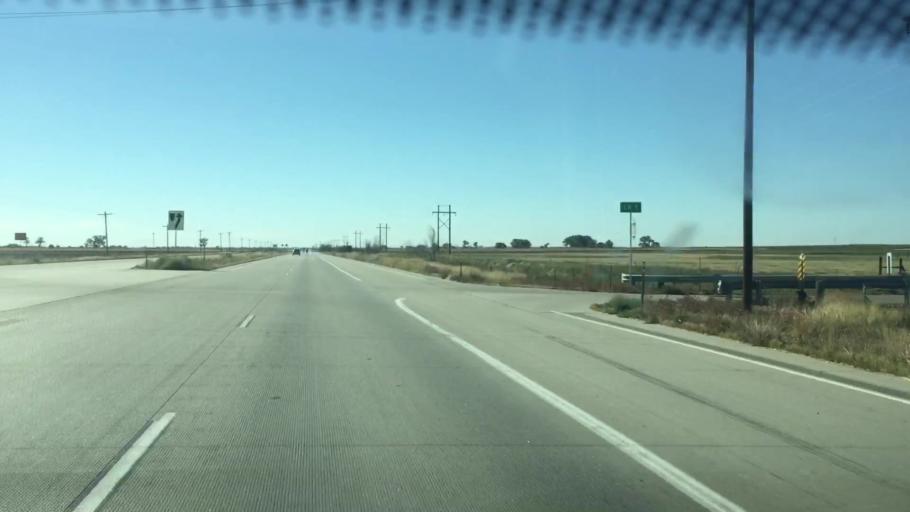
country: US
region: Colorado
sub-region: Prowers County
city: Lamar
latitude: 38.1108
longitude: -102.6681
